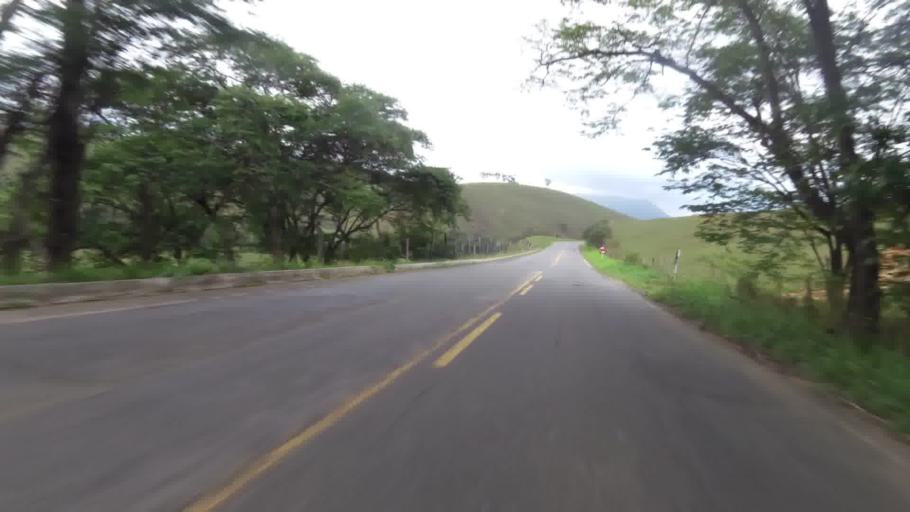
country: BR
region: Espirito Santo
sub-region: Alfredo Chaves
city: Alfredo Chaves
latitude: -20.6620
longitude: -40.7134
